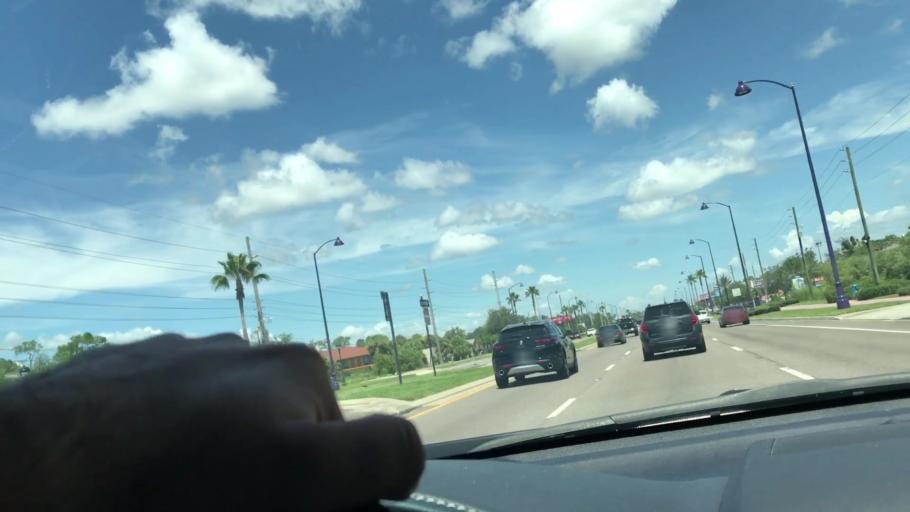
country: US
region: Florida
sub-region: Osceola County
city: Kissimmee
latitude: 28.3077
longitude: -81.4641
